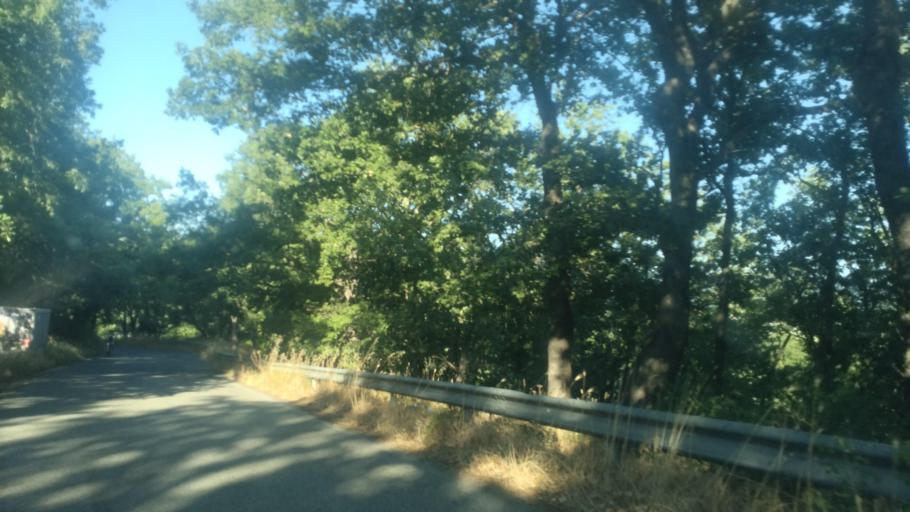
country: IT
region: Calabria
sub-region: Provincia di Catanzaro
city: Squillace
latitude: 38.7736
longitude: 16.5098
